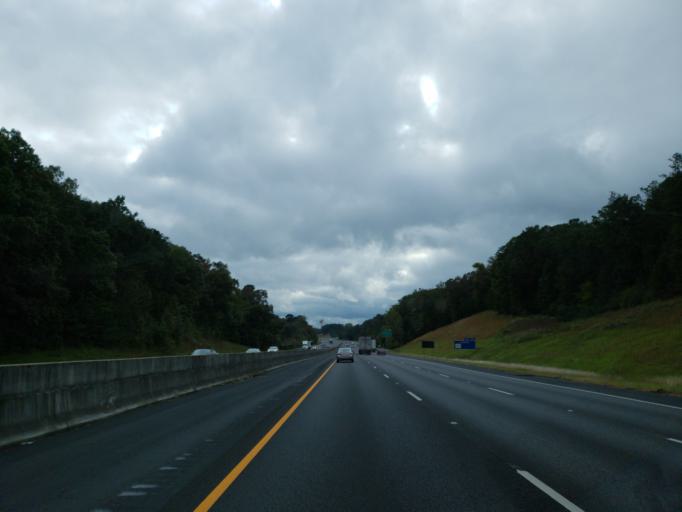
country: US
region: Alabama
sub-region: Tuscaloosa County
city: Lake View
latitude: 33.2921
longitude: -87.0794
